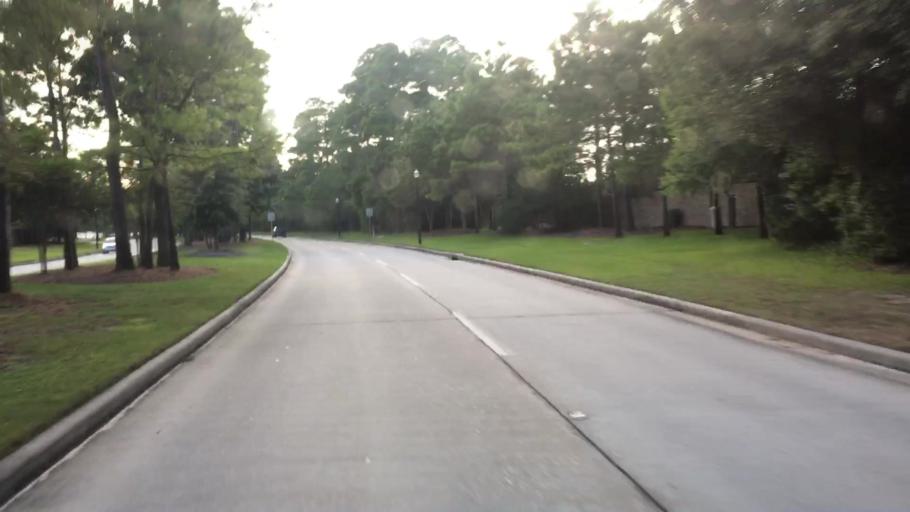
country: US
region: Texas
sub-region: Harris County
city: Atascocita
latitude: 29.9808
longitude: -95.1796
